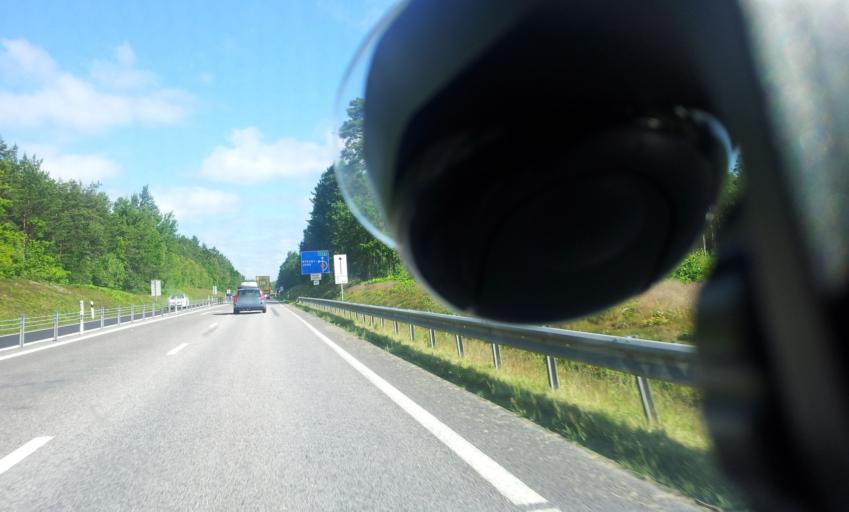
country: SE
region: Kalmar
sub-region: Kalmar Kommun
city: Lindsdal
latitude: 56.8259
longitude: 16.3680
